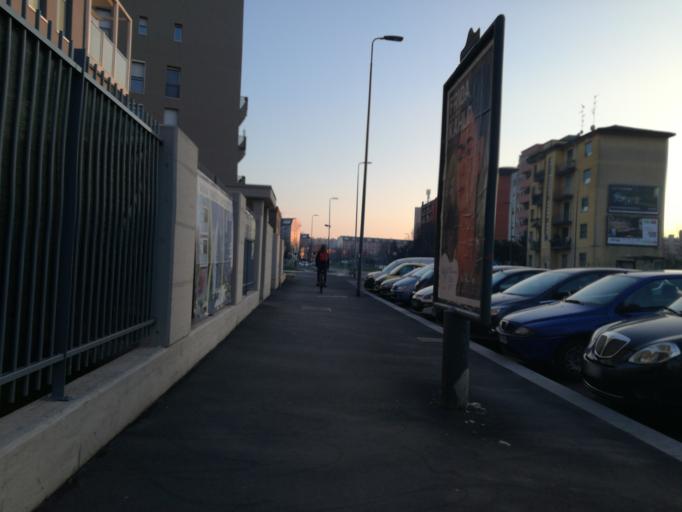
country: IT
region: Lombardy
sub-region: Citta metropolitana di Milano
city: Romano Banco
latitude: 45.4346
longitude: 9.1547
